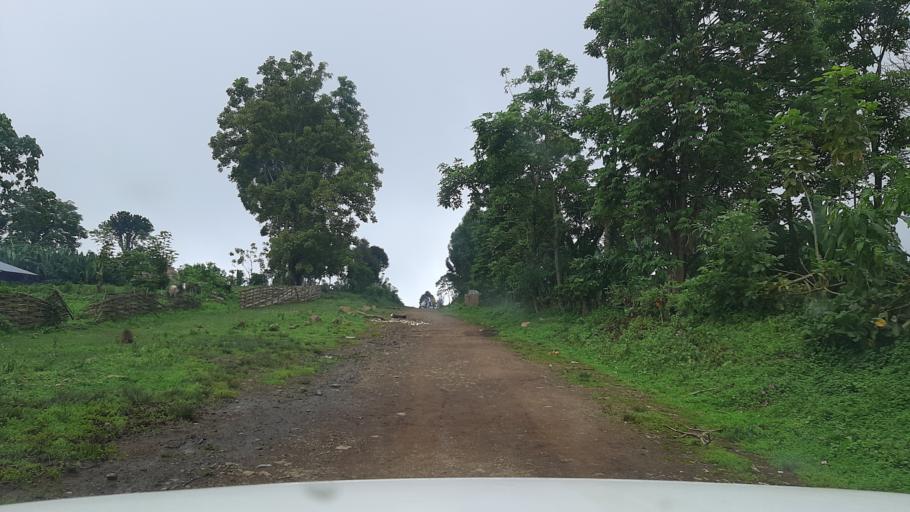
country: ET
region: Southern Nations, Nationalities, and People's Region
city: Bonga
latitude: 7.1119
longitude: 36.5329
